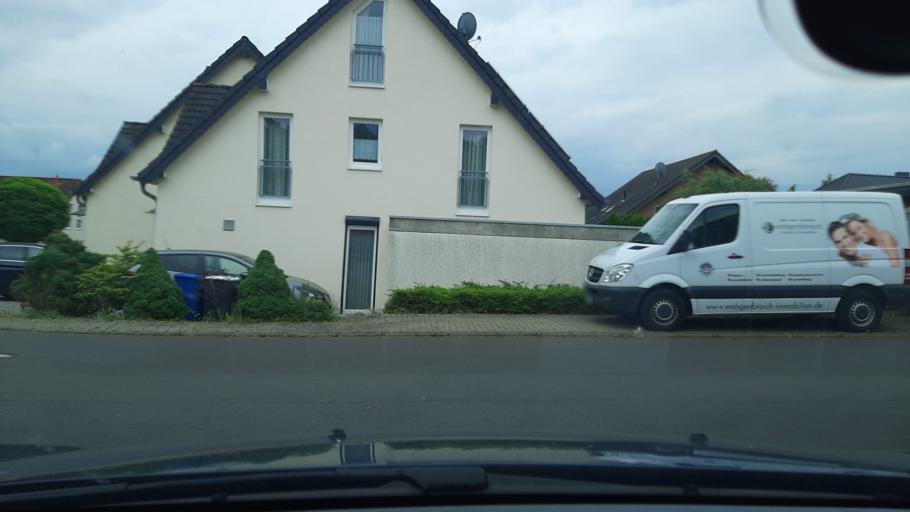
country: DE
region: North Rhine-Westphalia
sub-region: Regierungsbezirk Koln
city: Mechernich
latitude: 50.5995
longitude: 6.6562
